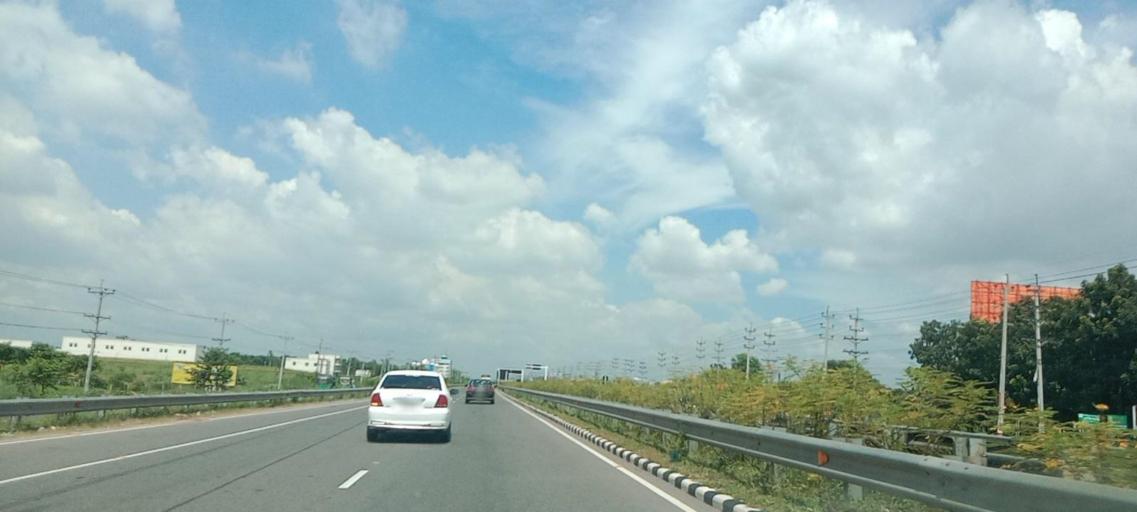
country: BD
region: Dhaka
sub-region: Dhaka
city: Dhaka
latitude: 23.6610
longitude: 90.3646
